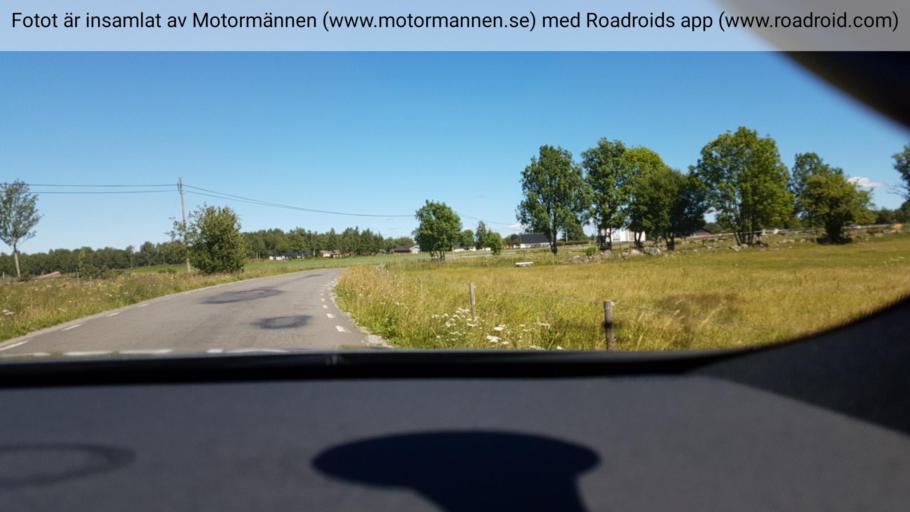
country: SE
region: Vaestra Goetaland
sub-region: Falkopings Kommun
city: Falkoeping
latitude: 58.0715
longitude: 13.5092
